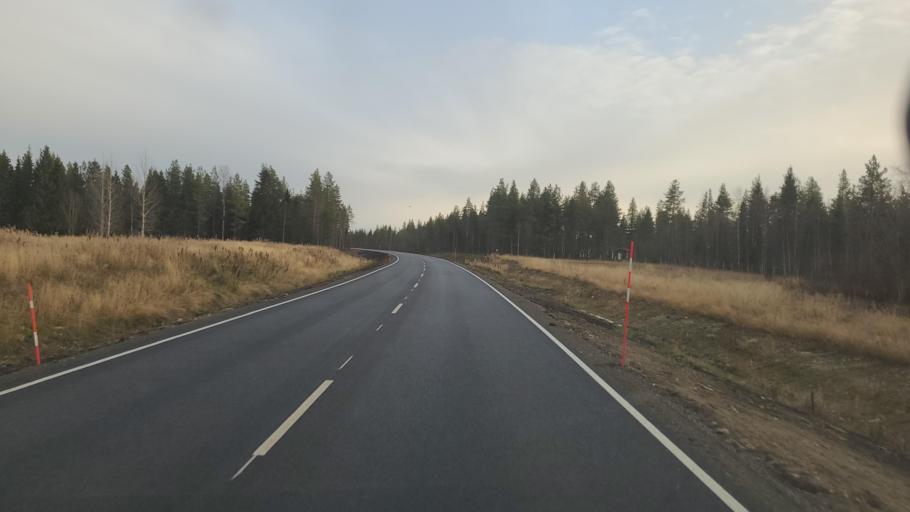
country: FI
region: Lapland
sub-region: Tunturi-Lappi
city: Kittilae
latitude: 67.8733
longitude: 24.8949
